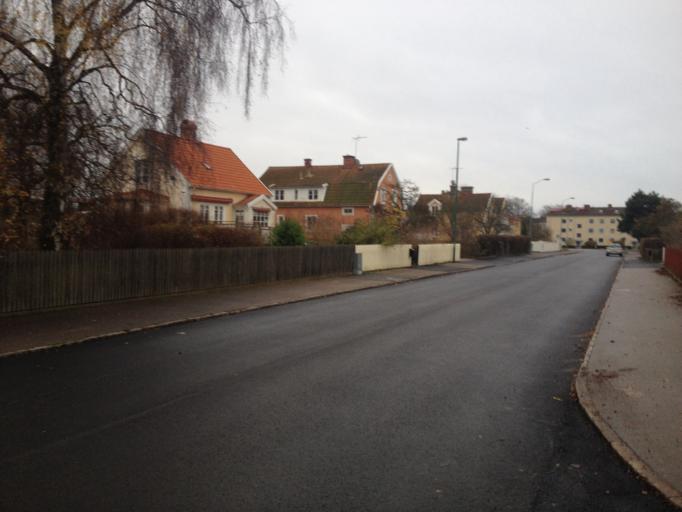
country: SE
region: Kalmar
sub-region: Kalmar Kommun
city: Kalmar
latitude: 56.6757
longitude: 16.3523
